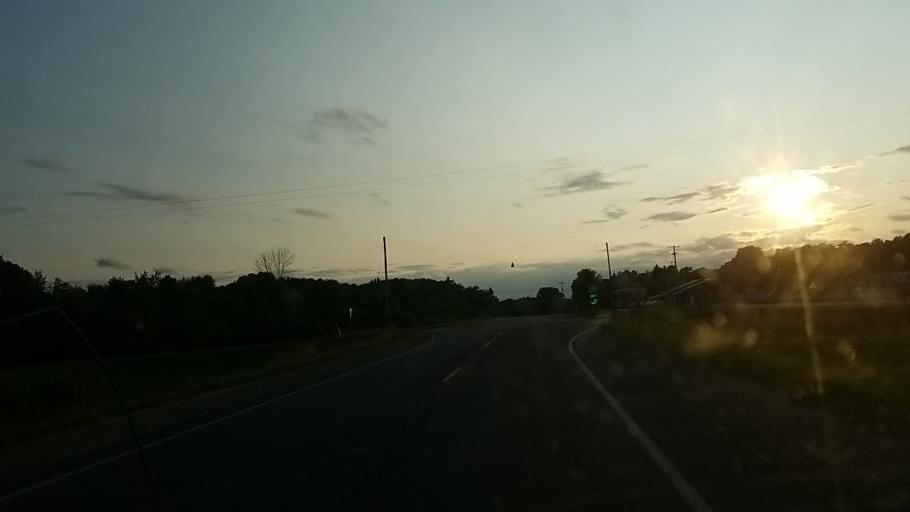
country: US
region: Michigan
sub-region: Newaygo County
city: Newaygo
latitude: 43.3959
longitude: -85.6417
